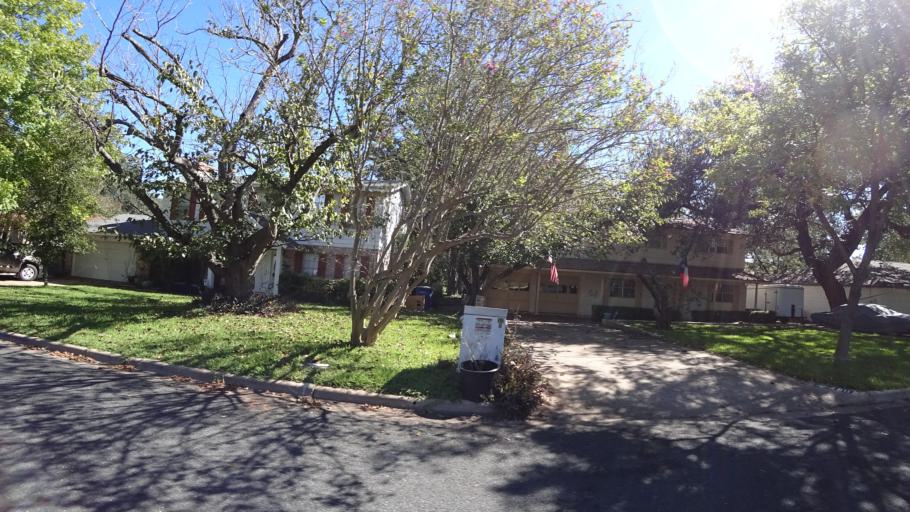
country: US
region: Texas
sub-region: Travis County
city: Rollingwood
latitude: 30.2247
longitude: -97.7957
